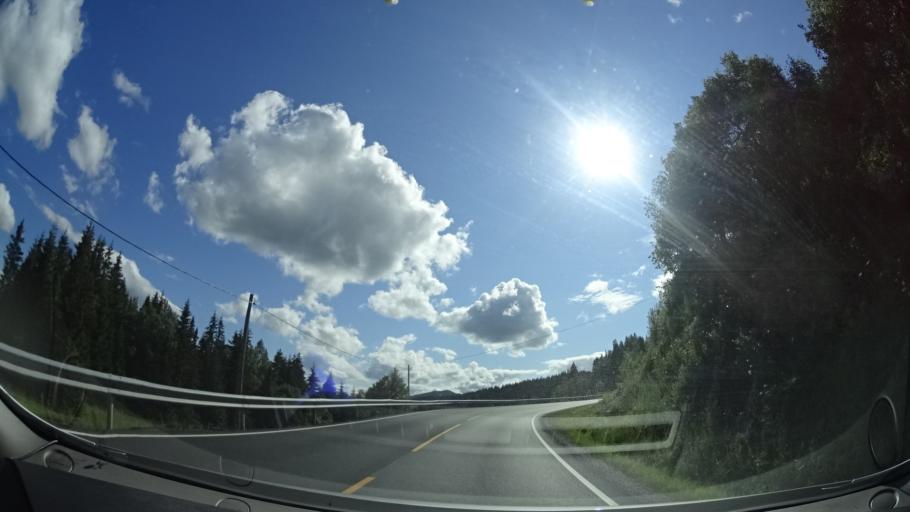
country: NO
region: Sor-Trondelag
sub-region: Snillfjord
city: Krokstadora
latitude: 63.2370
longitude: 9.5913
